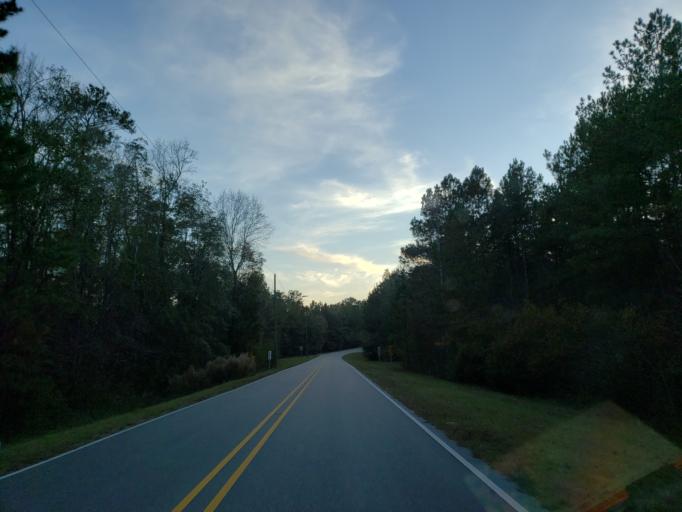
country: US
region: Mississippi
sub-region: Forrest County
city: Hattiesburg
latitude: 31.2659
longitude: -89.3103
